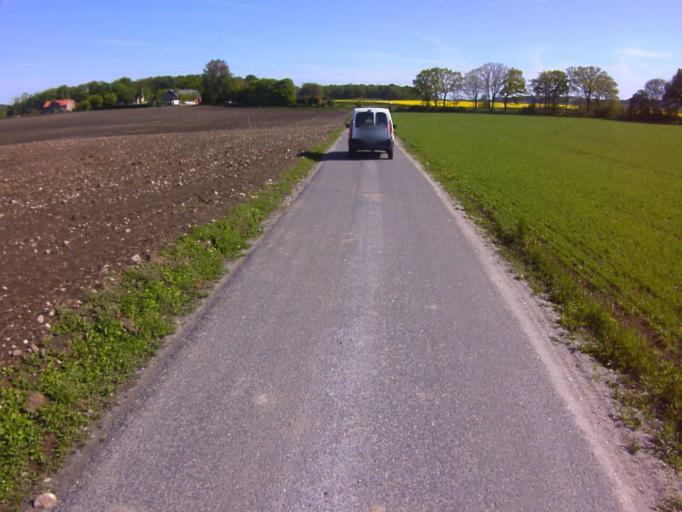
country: SE
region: Blekinge
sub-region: Solvesborgs Kommun
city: Soelvesborg
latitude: 56.0707
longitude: 14.6184
